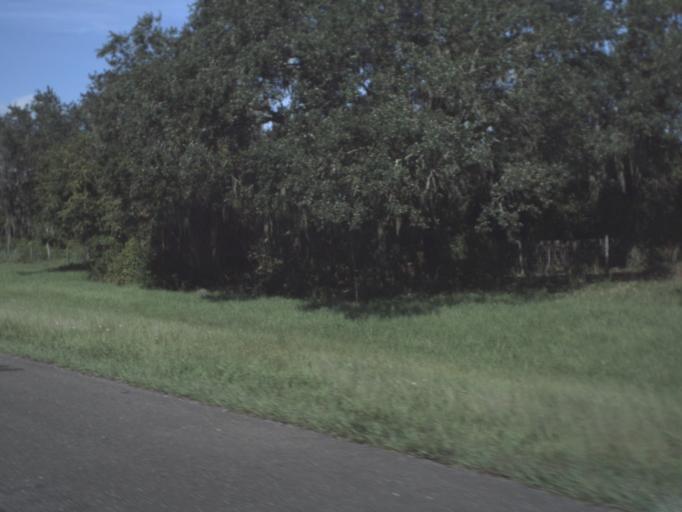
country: US
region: Florida
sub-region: Hillsborough County
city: Ruskin
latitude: 27.6444
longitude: -82.4568
